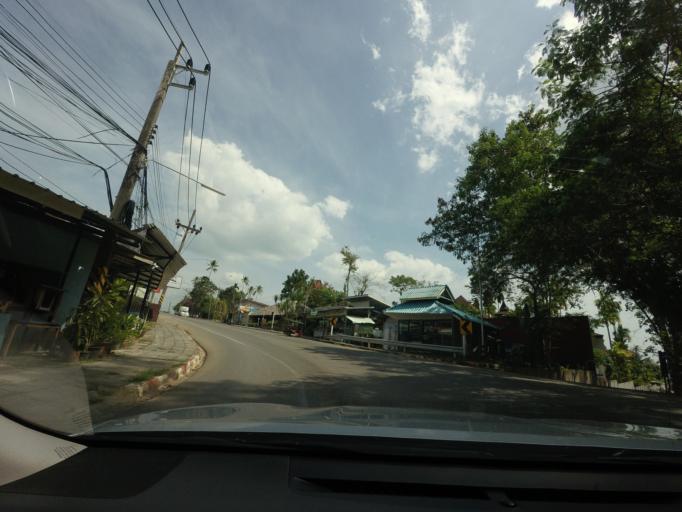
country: TH
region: Phangnga
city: Ban Ao Nang
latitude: 8.0557
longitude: 98.7501
